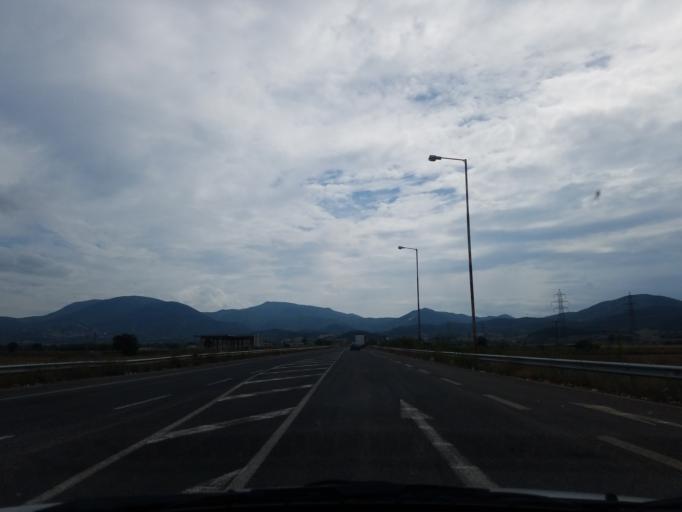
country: GR
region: Central Greece
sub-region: Nomos Fthiotidos
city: Domokos
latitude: 39.0416
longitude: 22.3533
